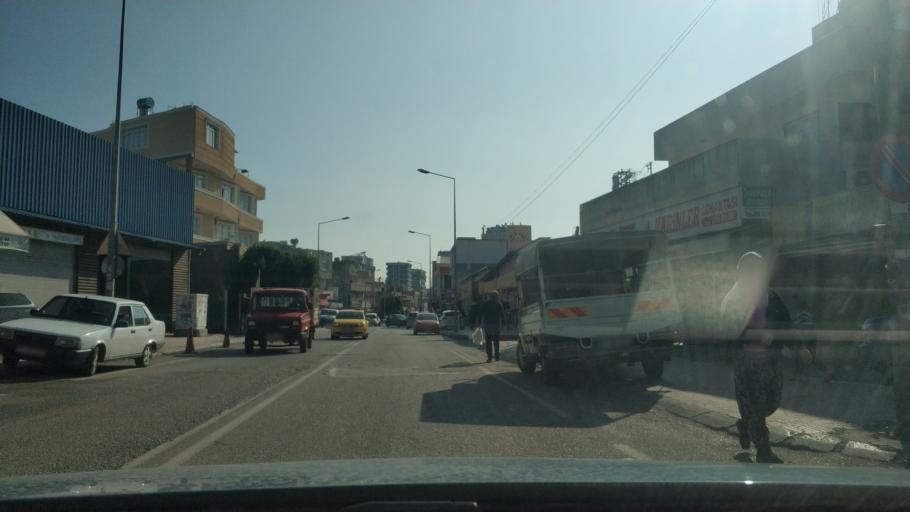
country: TR
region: Adana
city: Seyhan
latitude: 37.0193
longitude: 35.2968
